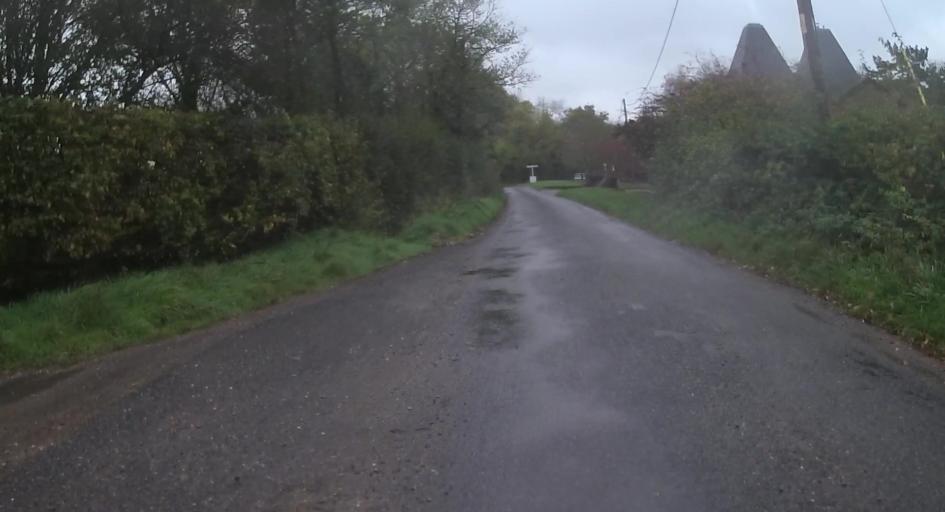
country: GB
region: England
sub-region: Surrey
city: Farnham
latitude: 51.2010
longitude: -0.8518
